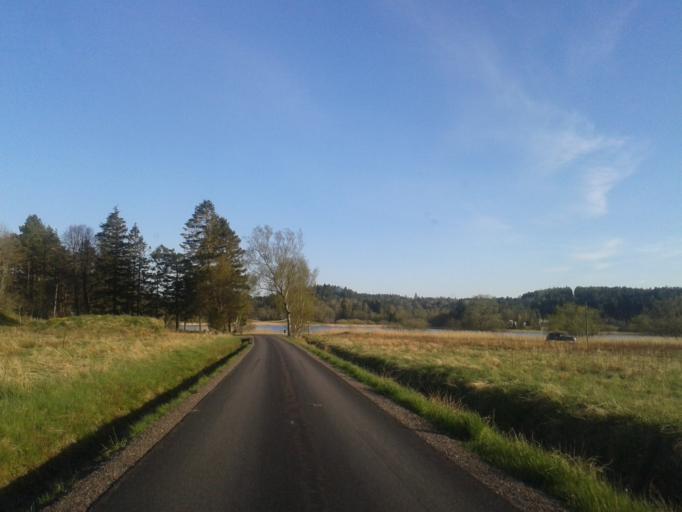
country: SE
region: Vaestra Goetaland
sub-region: Ale Kommun
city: Alafors
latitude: 57.8930
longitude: 12.0828
